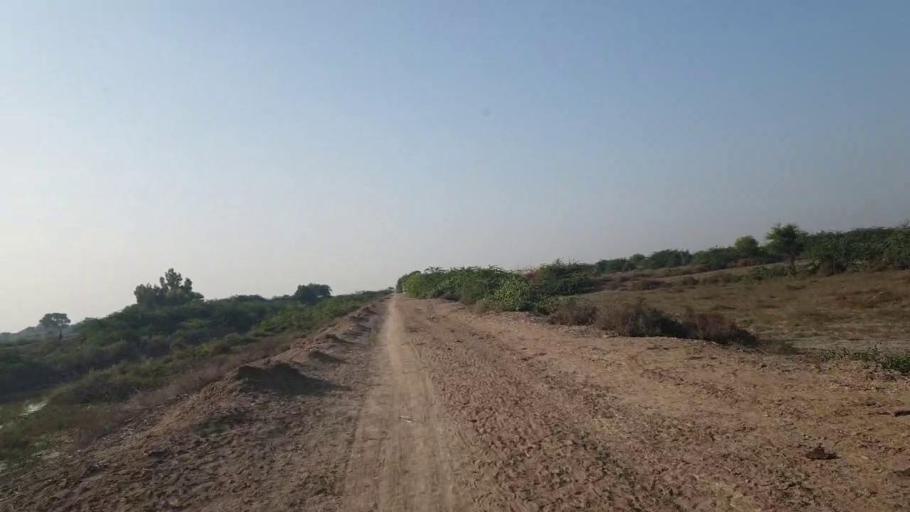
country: PK
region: Sindh
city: Badin
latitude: 24.4711
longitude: 68.7405
